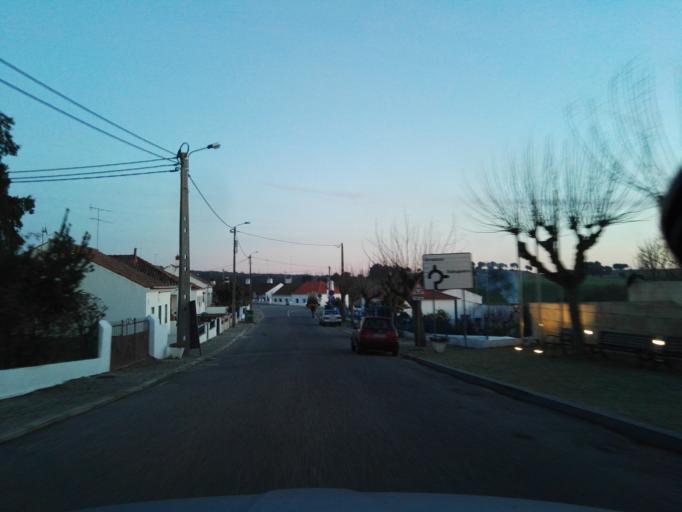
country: PT
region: Evora
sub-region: Arraiolos
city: Arraiolos
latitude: 38.7404
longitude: -8.0760
